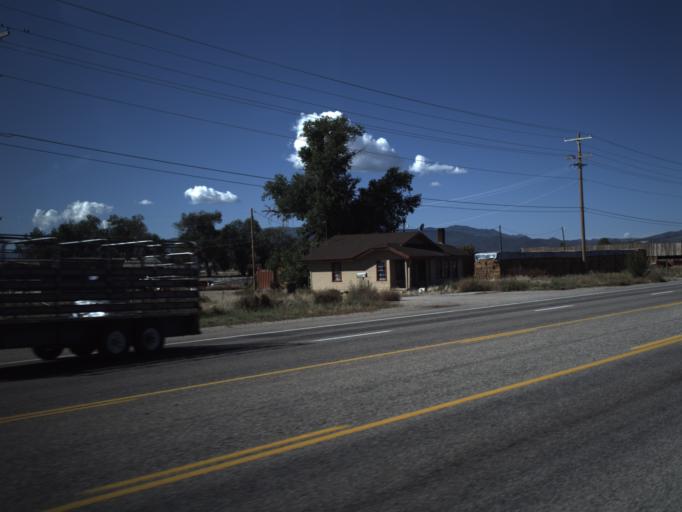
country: US
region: Utah
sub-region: Iron County
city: Cedar City
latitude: 37.6851
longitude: -113.1224
